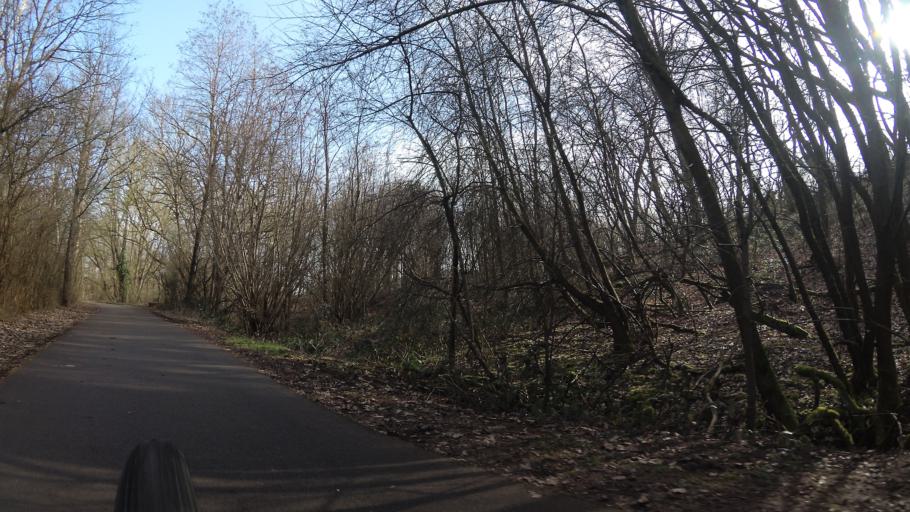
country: DE
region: Saarland
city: Saarlouis
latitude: 49.2967
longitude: 6.7357
